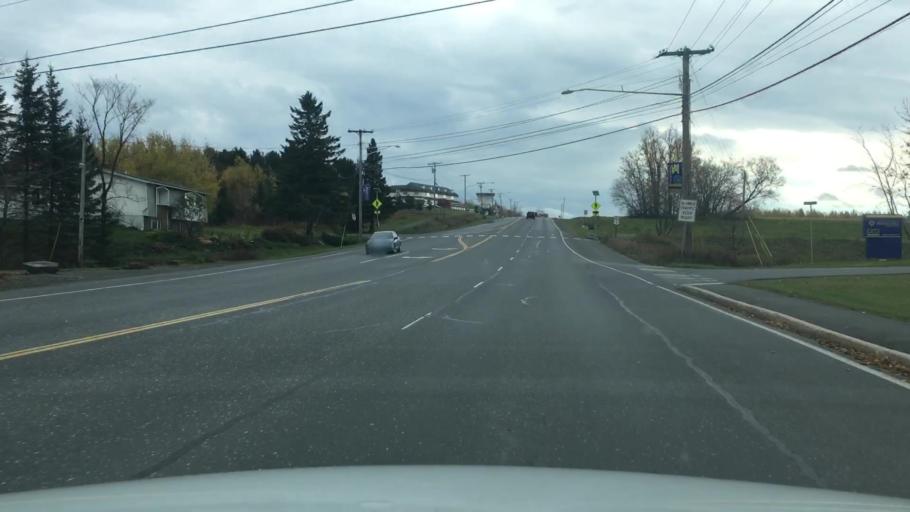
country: US
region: Maine
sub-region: Aroostook County
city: Presque Isle
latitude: 46.6705
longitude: -68.0139
